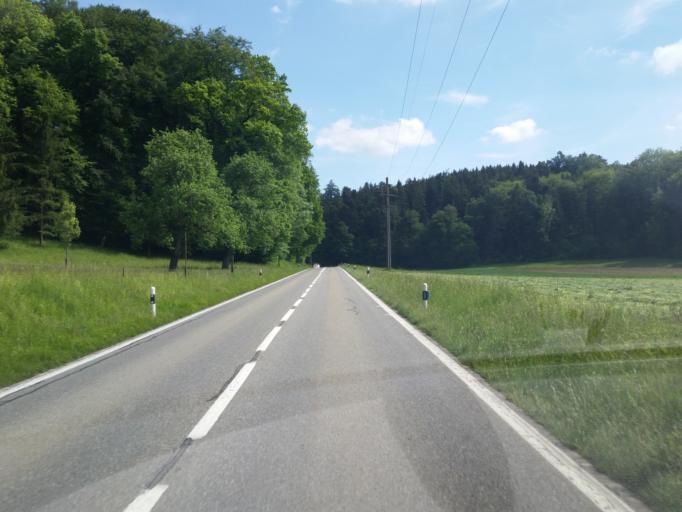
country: CH
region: Aargau
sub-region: Bezirk Bremgarten
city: Bremgarten
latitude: 47.3252
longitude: 8.3475
